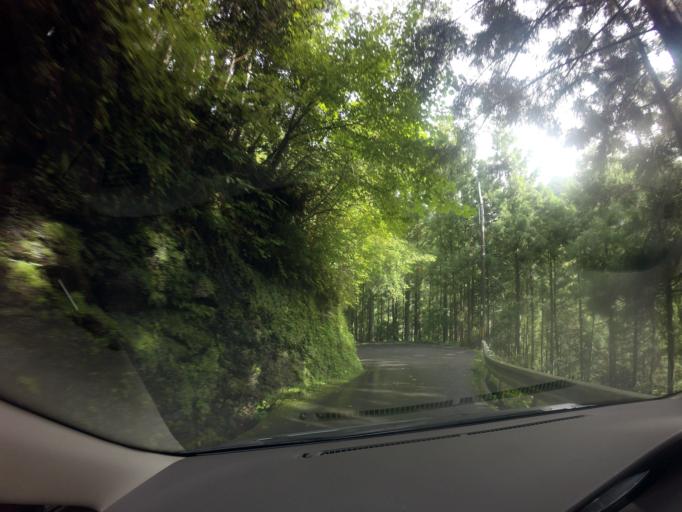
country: JP
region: Wakayama
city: Shingu
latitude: 33.9687
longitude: 135.8085
